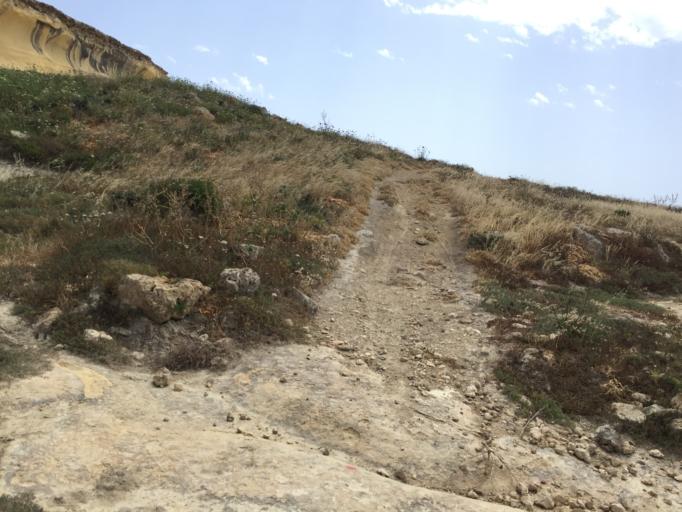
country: MT
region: L-Gharb
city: Gharb
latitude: 36.0774
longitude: 14.2036
